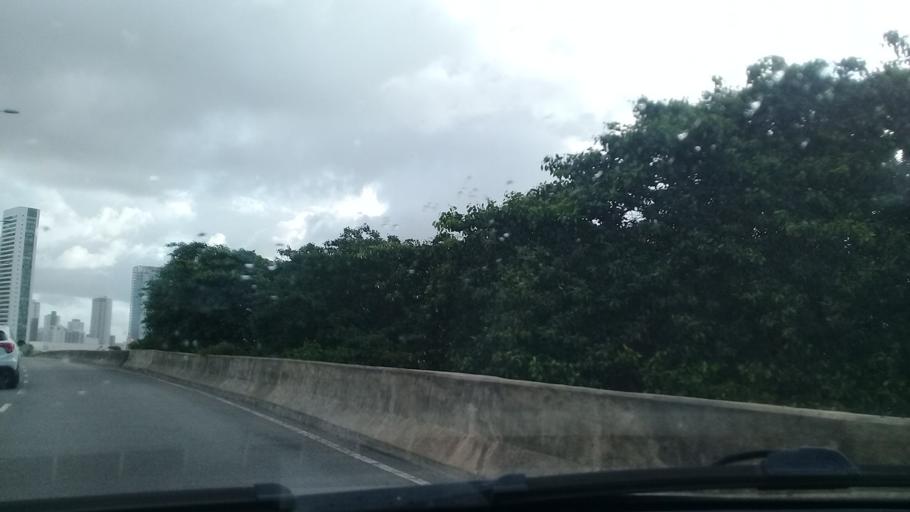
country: BR
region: Pernambuco
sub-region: Recife
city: Recife
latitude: -8.1117
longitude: -34.9017
